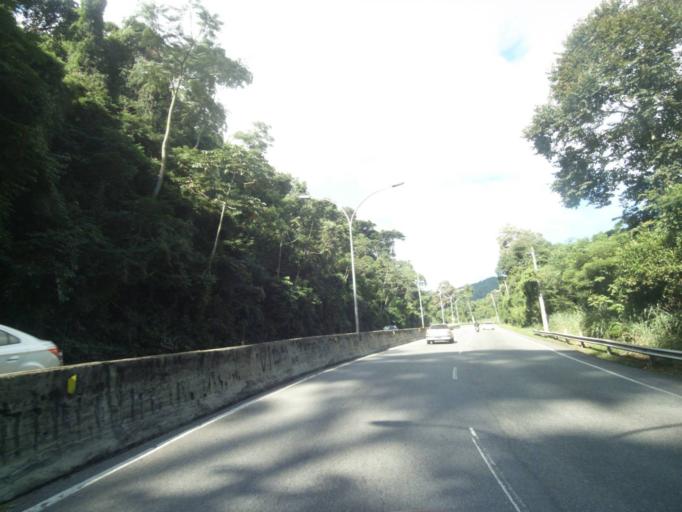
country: BR
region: Rio de Janeiro
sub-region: Rio De Janeiro
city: Rio de Janeiro
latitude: -22.9229
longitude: -43.3100
